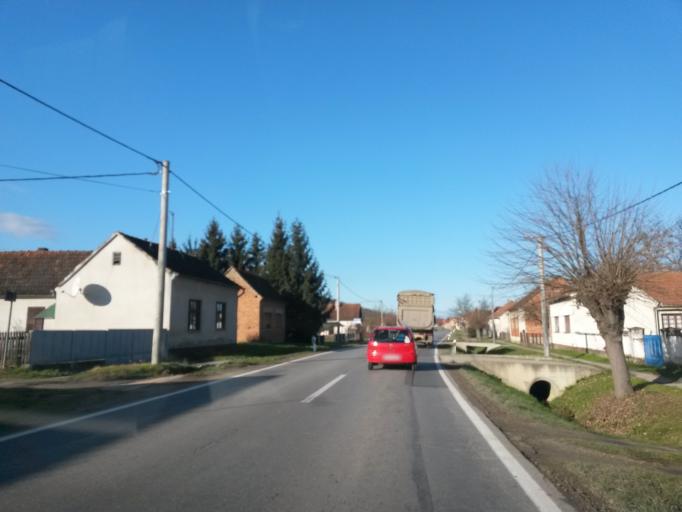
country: HR
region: Virovitick-Podravska
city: Suhopolje
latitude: 45.7524
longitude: 17.5833
